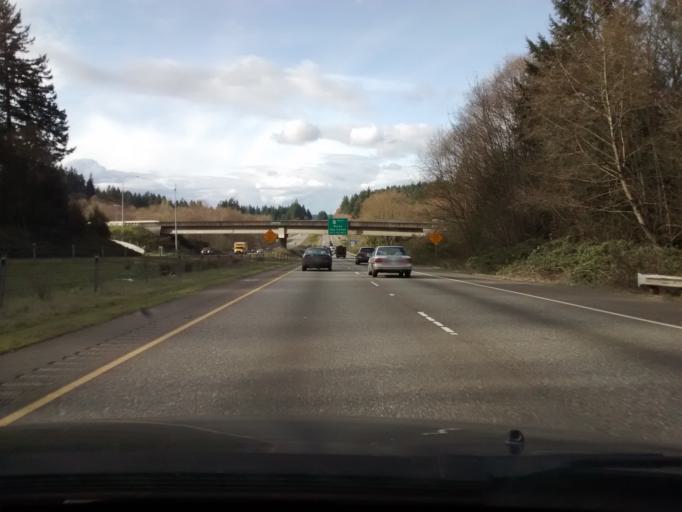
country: US
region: Washington
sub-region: Pierce County
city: Canterwood
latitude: 47.3573
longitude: -122.6138
